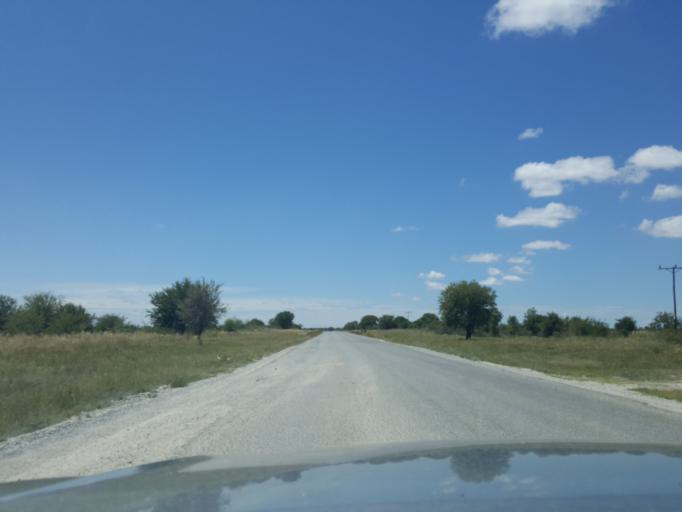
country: BW
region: Central
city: Nata
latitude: -20.1565
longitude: 25.8329
